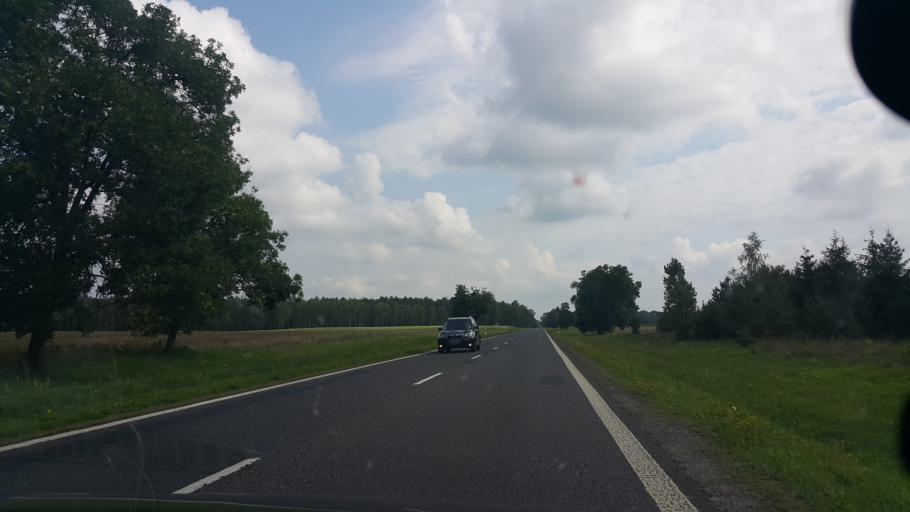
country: PL
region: Lublin Voivodeship
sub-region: Powiat wlodawski
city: Hansk
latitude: 51.4784
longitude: 23.3353
